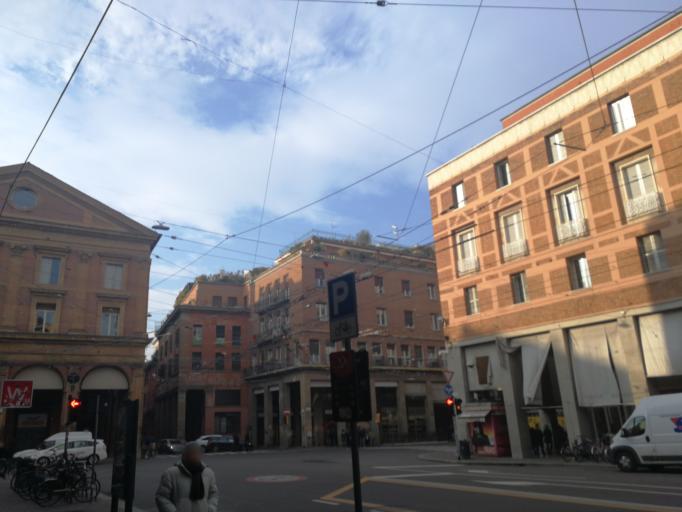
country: IT
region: Emilia-Romagna
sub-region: Provincia di Bologna
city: Bologna
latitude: 44.4958
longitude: 11.3375
